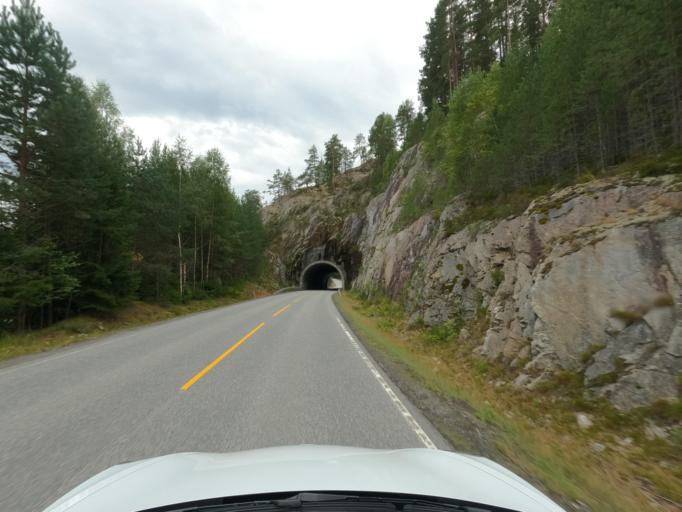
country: NO
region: Telemark
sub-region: Hjartdal
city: Sauland
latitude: 59.7367
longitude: 9.0198
